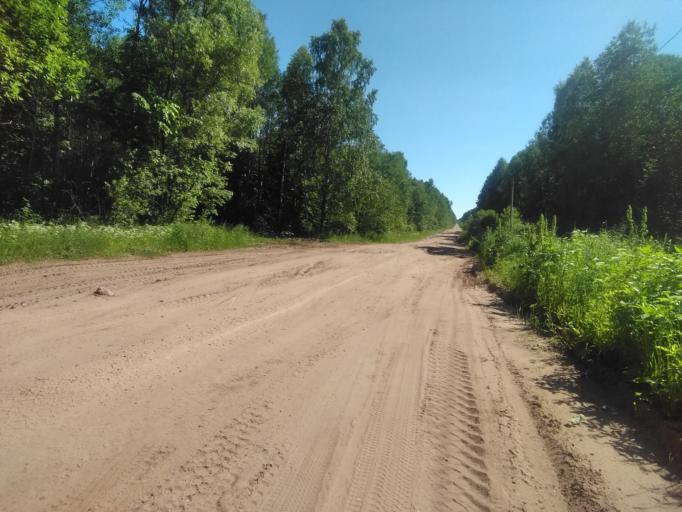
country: RU
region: Bashkortostan
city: Amzya
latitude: 56.4576
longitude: 54.5404
